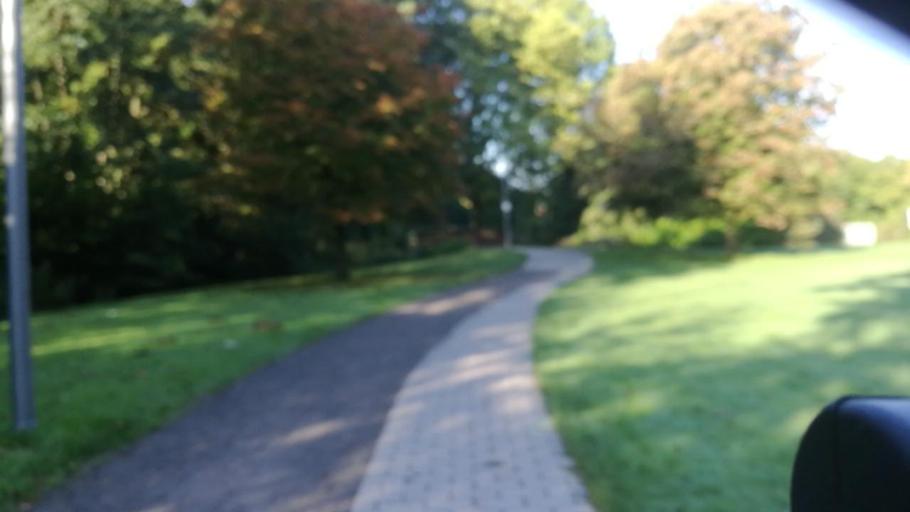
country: DE
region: North Rhine-Westphalia
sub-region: Regierungsbezirk Detmold
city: Bielefeld
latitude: 52.0017
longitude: 8.5878
